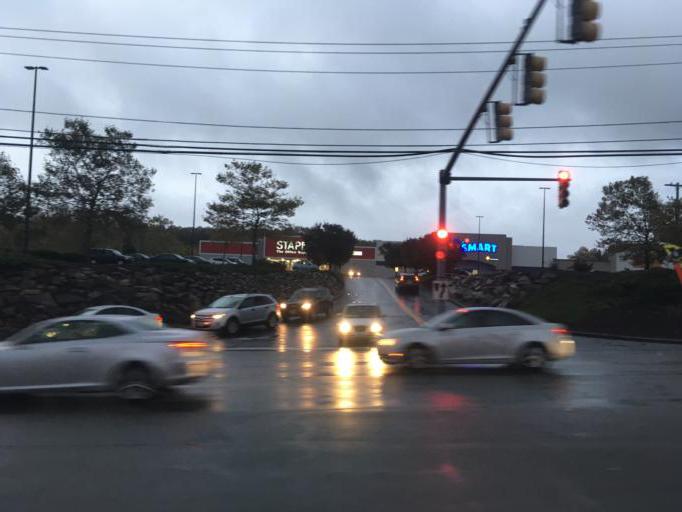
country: US
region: Rhode Island
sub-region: Kent County
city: West Warwick
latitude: 41.7065
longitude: -71.4925
